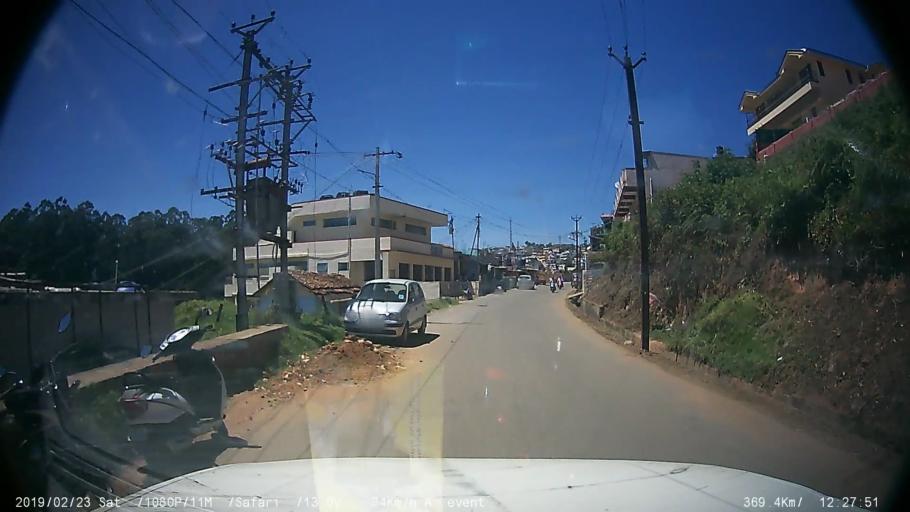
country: IN
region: Tamil Nadu
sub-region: Nilgiri
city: Wellington
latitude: 11.3478
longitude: 76.7842
